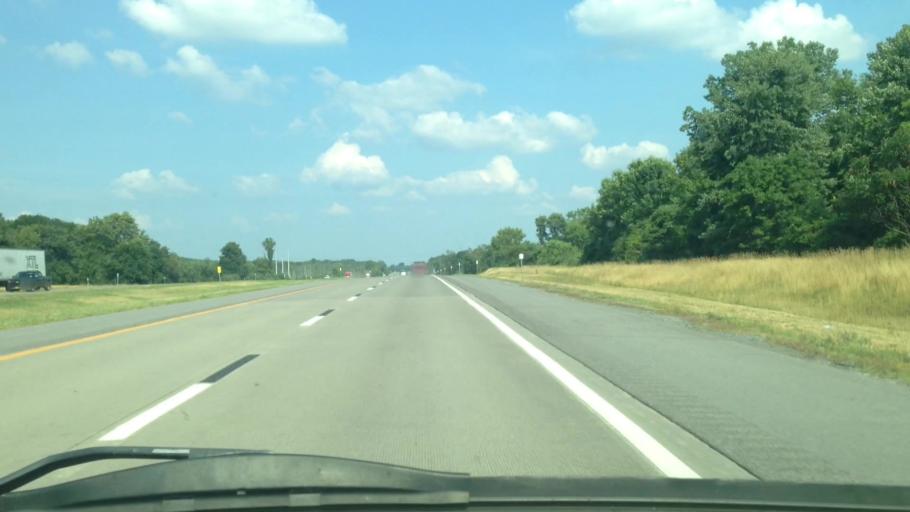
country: US
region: New York
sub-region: Onondaga County
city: Peru
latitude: 43.0893
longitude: -76.3717
